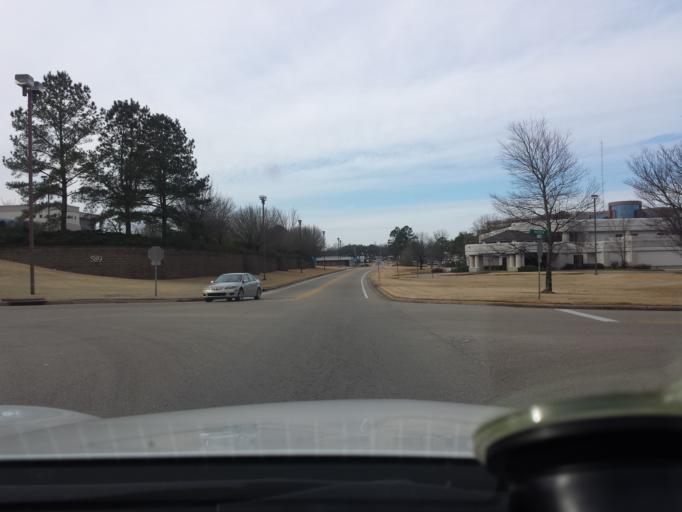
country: US
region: Mississippi
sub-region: Lee County
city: Tupelo
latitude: 34.2385
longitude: -88.7131
